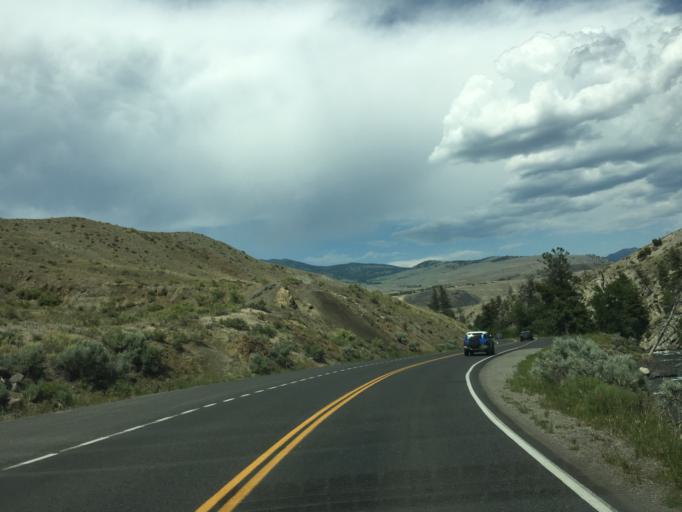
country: US
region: Montana
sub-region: Gallatin County
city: West Yellowstone
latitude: 45.0121
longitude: -110.6945
